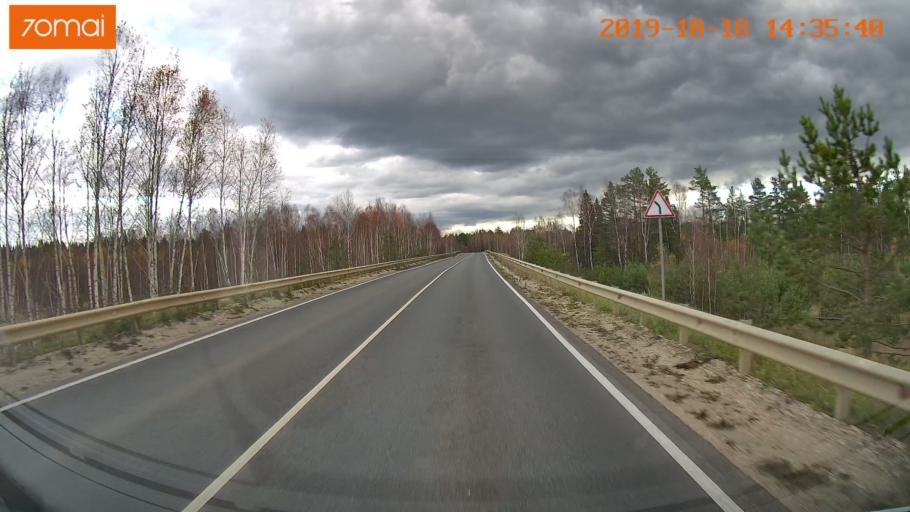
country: RU
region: Vladimir
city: Velikodvorskiy
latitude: 55.2223
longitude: 40.6430
